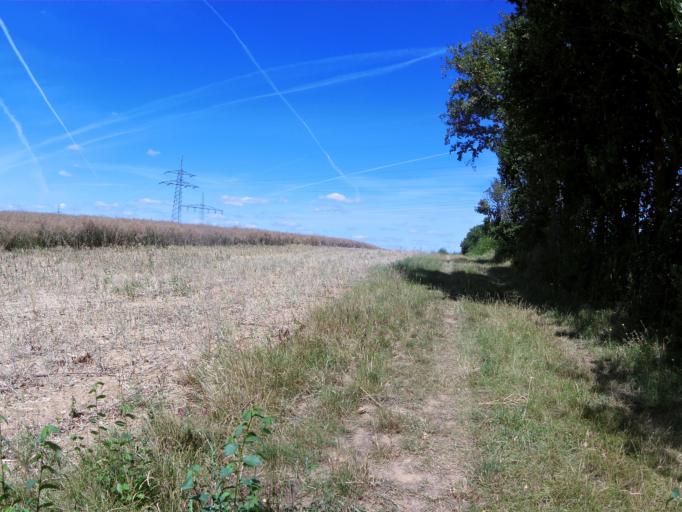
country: DE
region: Bavaria
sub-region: Regierungsbezirk Unterfranken
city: Hettstadt
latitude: 49.8131
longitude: 9.8323
